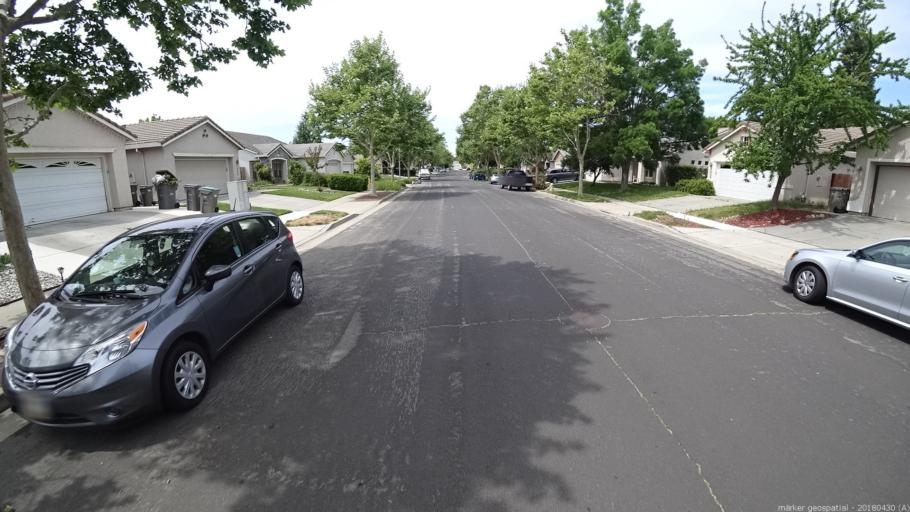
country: US
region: California
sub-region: Yolo County
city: West Sacramento
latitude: 38.5544
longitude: -121.5262
